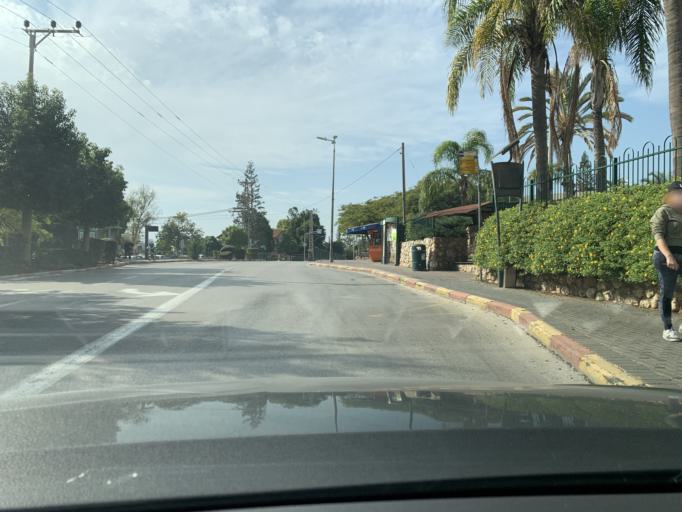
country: IL
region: Central District
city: Ganne Tiqwa
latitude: 32.0607
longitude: 34.8612
